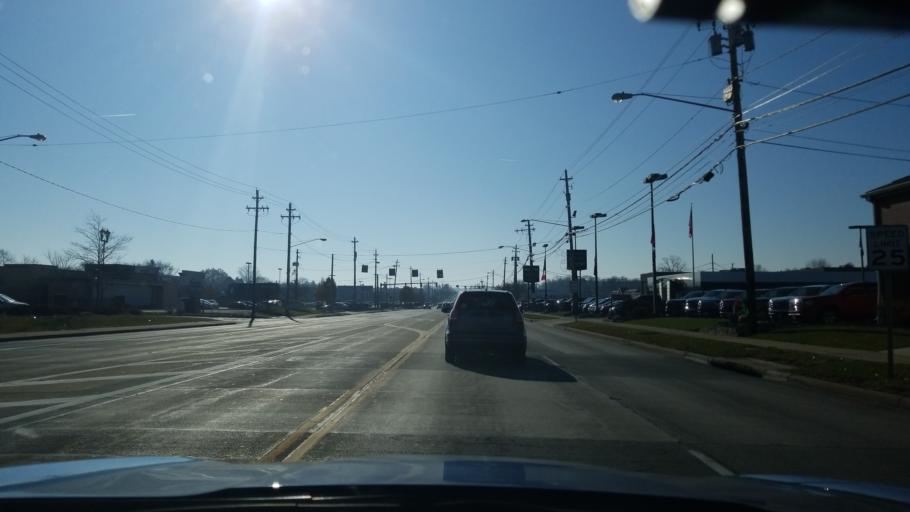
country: US
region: Ohio
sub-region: Cuyahoga County
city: Strongsville
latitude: 41.3137
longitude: -81.8352
